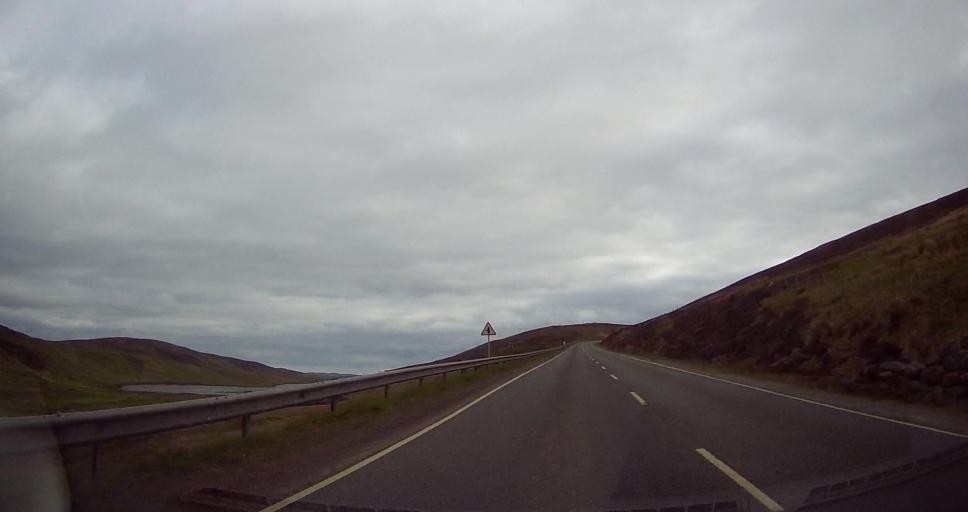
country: GB
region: Scotland
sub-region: Shetland Islands
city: Lerwick
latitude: 60.1621
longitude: -1.2202
